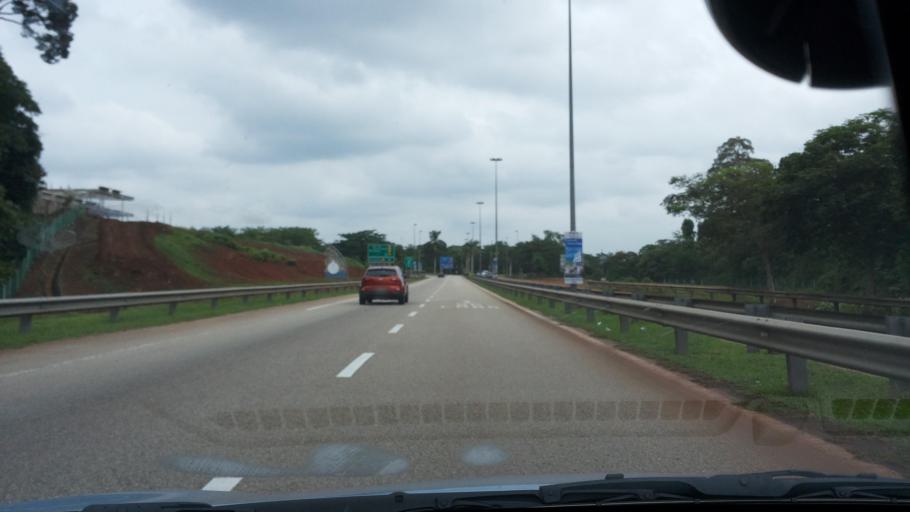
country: MY
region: Pahang
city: Kuantan
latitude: 3.8672
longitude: 103.2407
